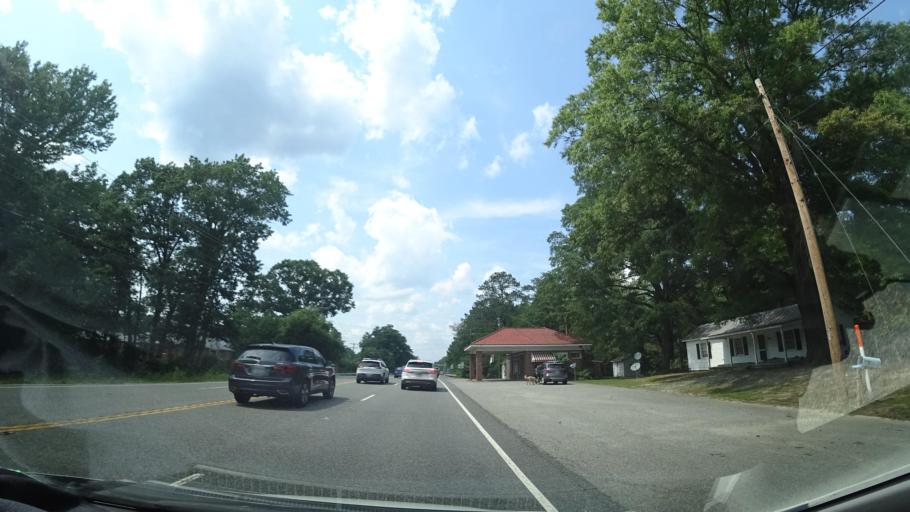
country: US
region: Virginia
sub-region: Hanover County
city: Ashland
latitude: 37.9287
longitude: -77.4793
